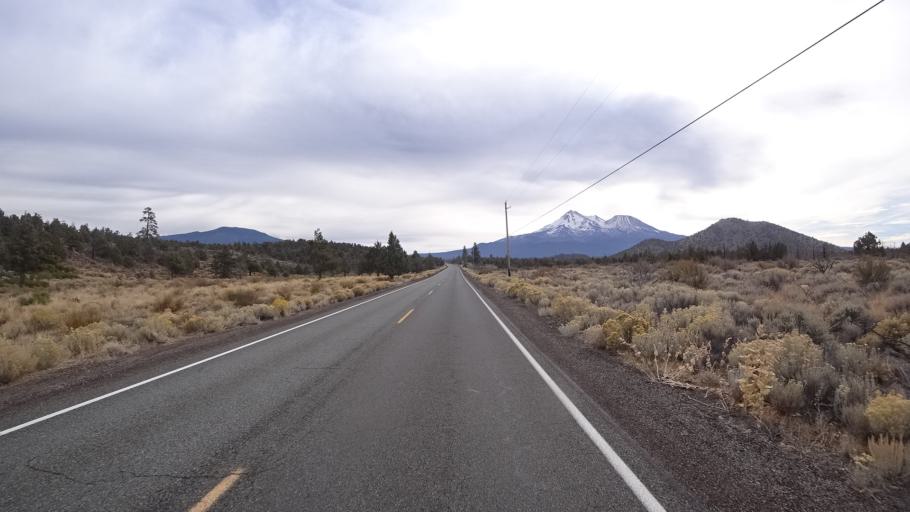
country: US
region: California
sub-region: Siskiyou County
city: Weed
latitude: 41.5620
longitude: -122.2609
